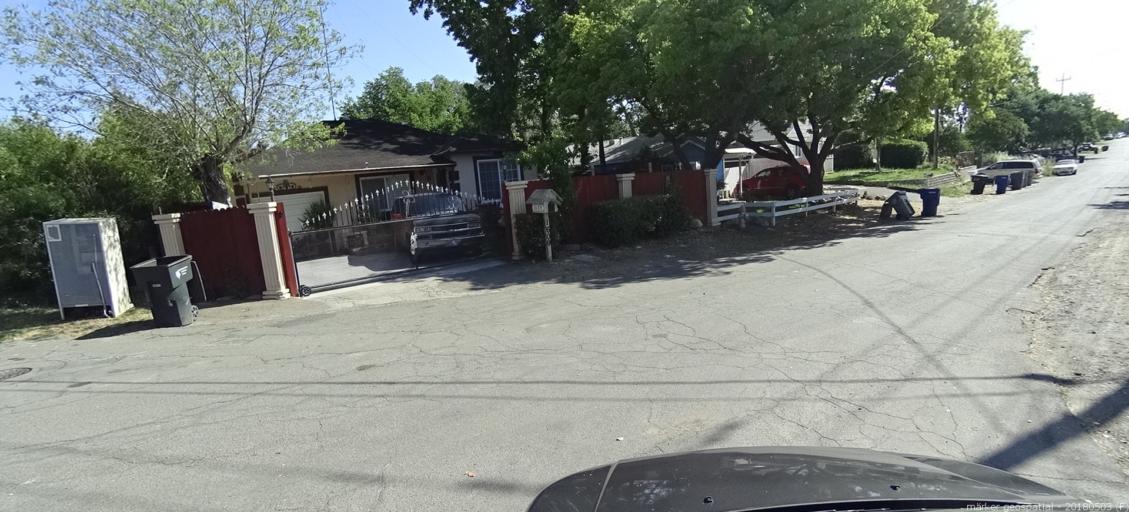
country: US
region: California
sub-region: Sacramento County
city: Arden-Arcade
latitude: 38.6220
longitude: -121.4299
